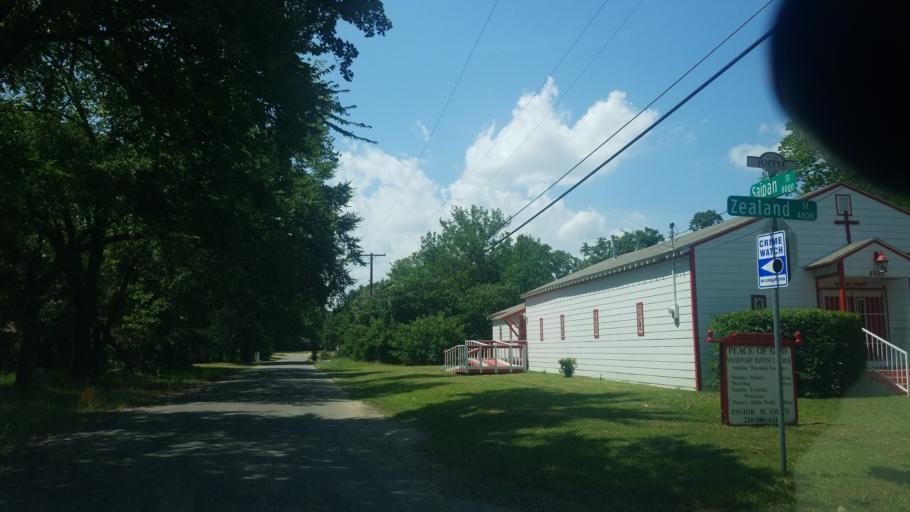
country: US
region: Texas
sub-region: Dallas County
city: Hutchins
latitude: 32.7152
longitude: -96.7428
